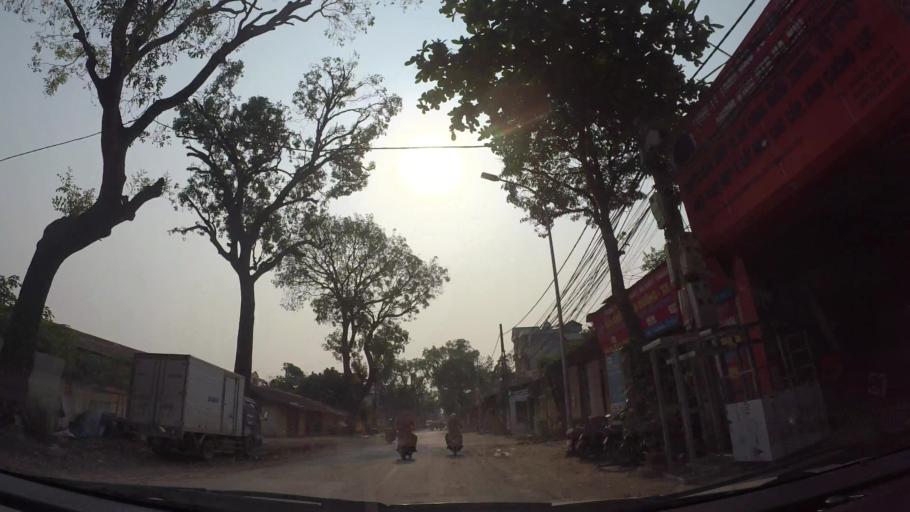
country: VN
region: Ha Noi
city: Ha Dong
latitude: 20.9958
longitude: 105.7491
